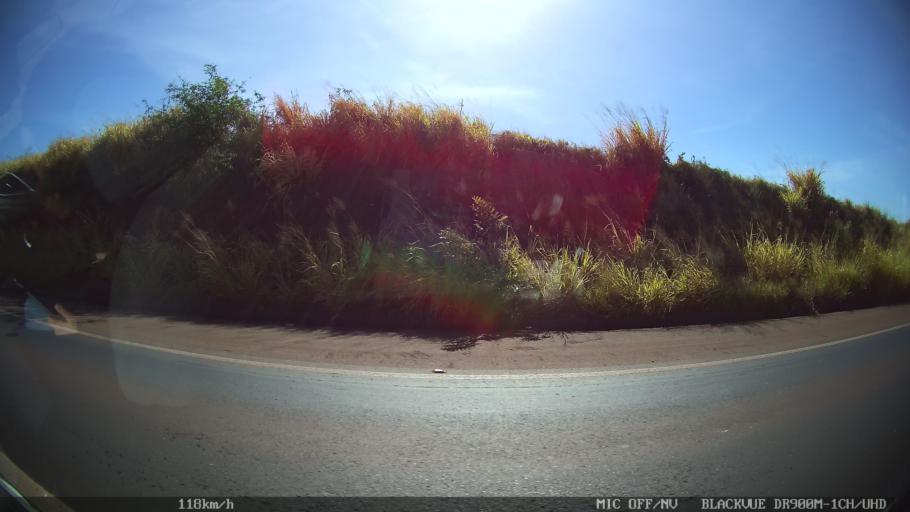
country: BR
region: Sao Paulo
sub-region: Barretos
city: Barretos
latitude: -20.5391
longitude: -48.6124
